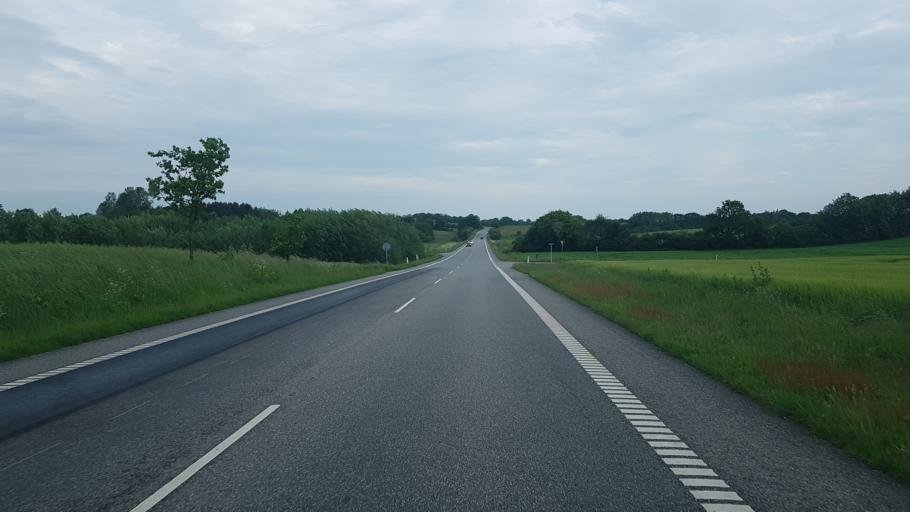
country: DK
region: South Denmark
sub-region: Vejen Kommune
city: Rodding
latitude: 55.3859
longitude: 9.0479
